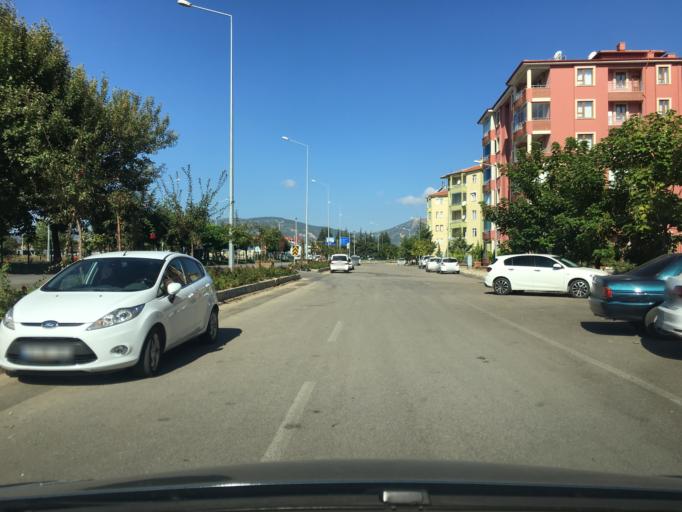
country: TR
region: Isparta
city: Isparta
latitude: 37.7910
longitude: 30.5463
